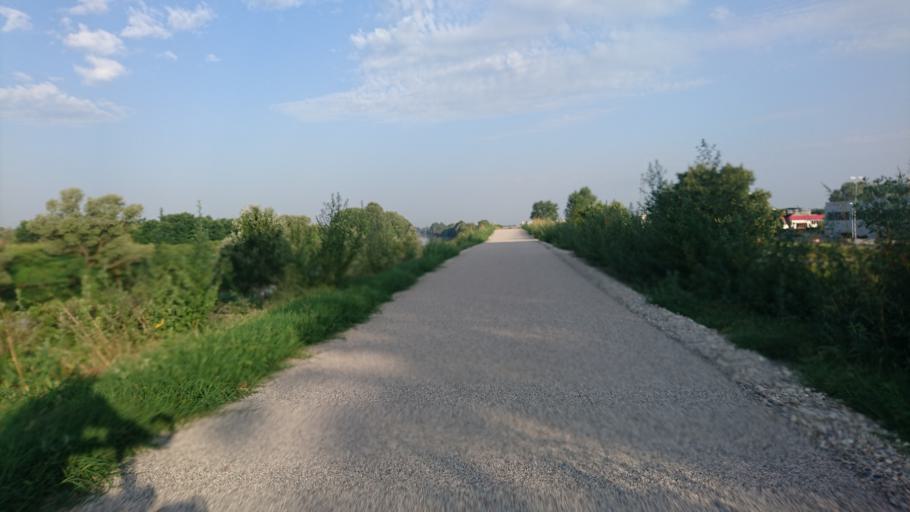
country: IT
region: Veneto
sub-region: Provincia di Padova
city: Oltre Brenta
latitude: 45.4179
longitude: 11.9833
